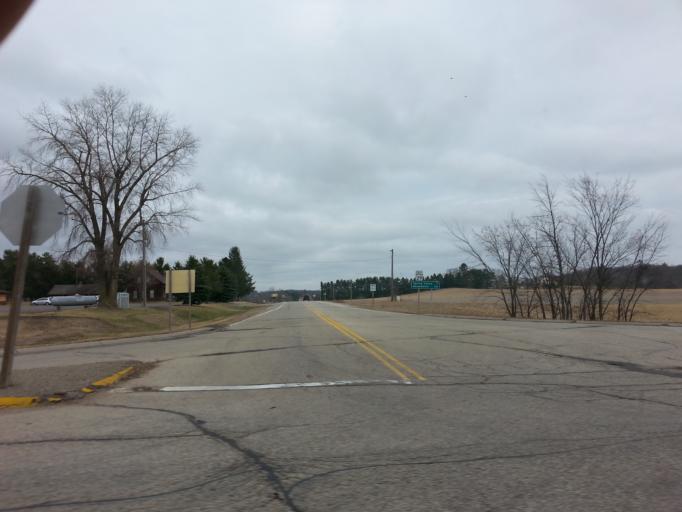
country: US
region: Wisconsin
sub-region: Saint Croix County
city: Baldwin
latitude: 44.8334
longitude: -92.3750
